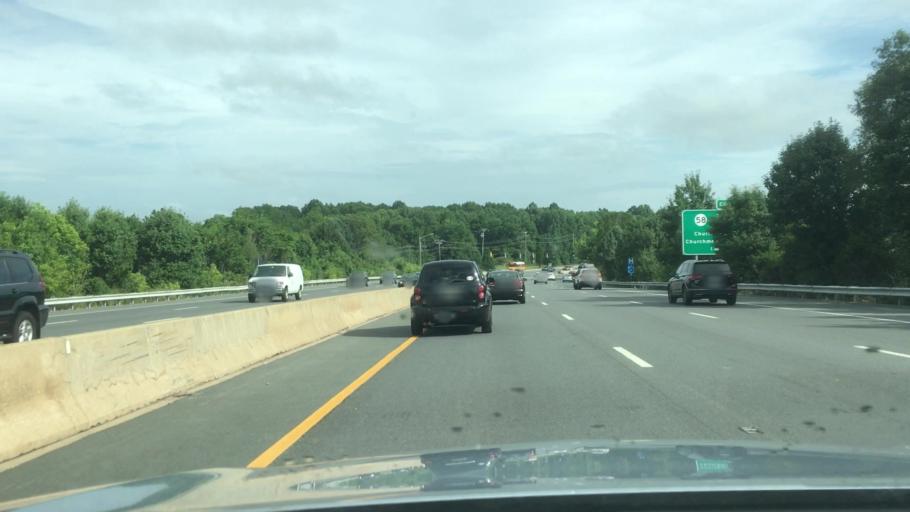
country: US
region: Delaware
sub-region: New Castle County
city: Newport
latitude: 39.7016
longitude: -75.6525
